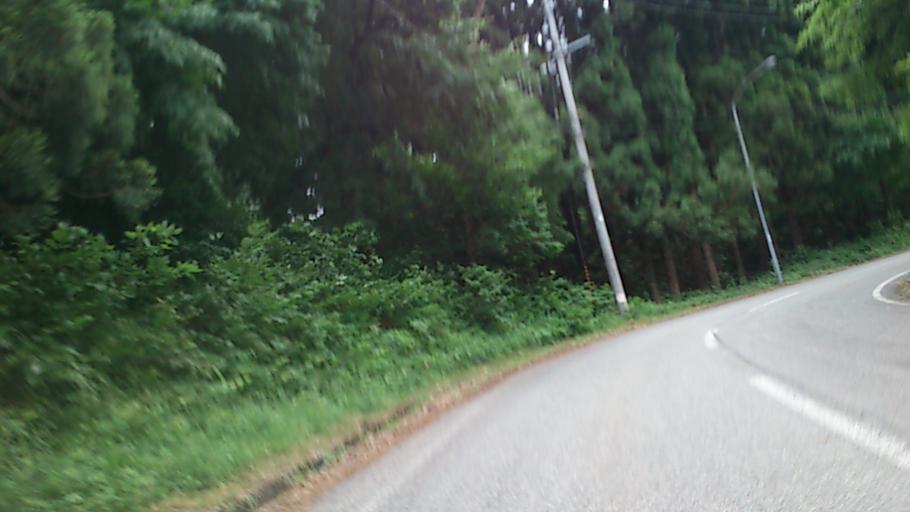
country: JP
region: Yamagata
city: Tsuruoka
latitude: 38.7878
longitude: 139.9787
